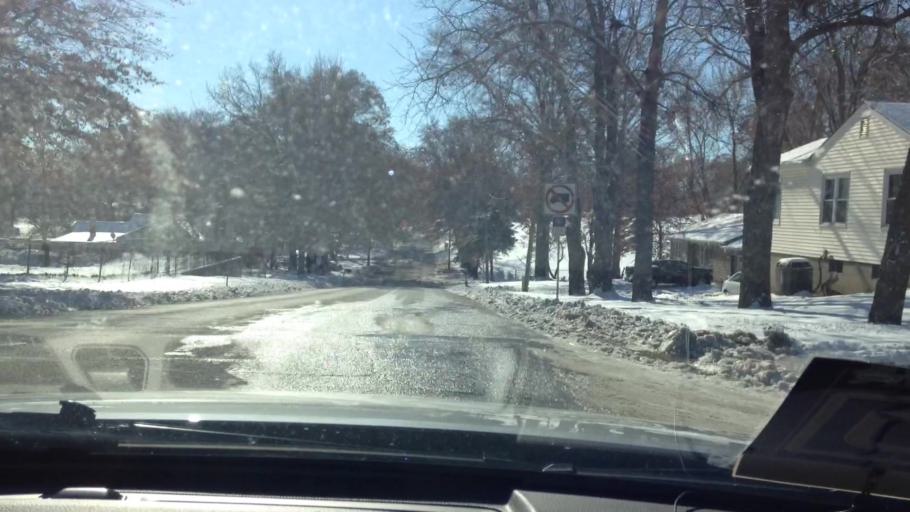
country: US
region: Kansas
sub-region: Leavenworth County
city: Leavenworth
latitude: 39.3008
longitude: -94.9209
